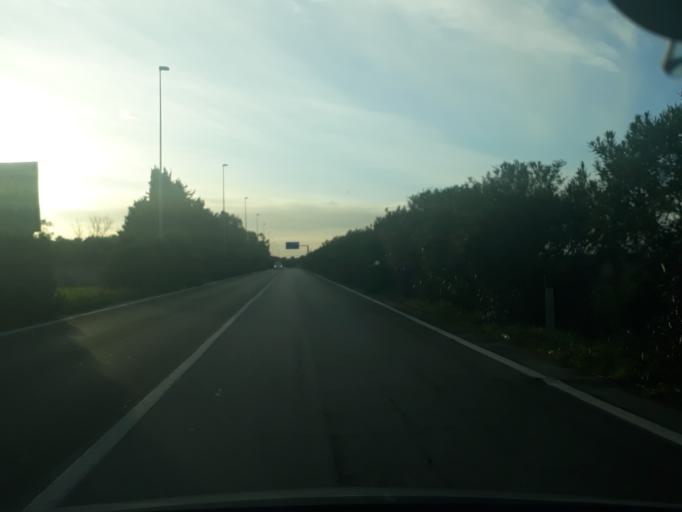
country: IT
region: Apulia
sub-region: Provincia di Brindisi
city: Brindisi
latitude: 40.6614
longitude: 17.9245
